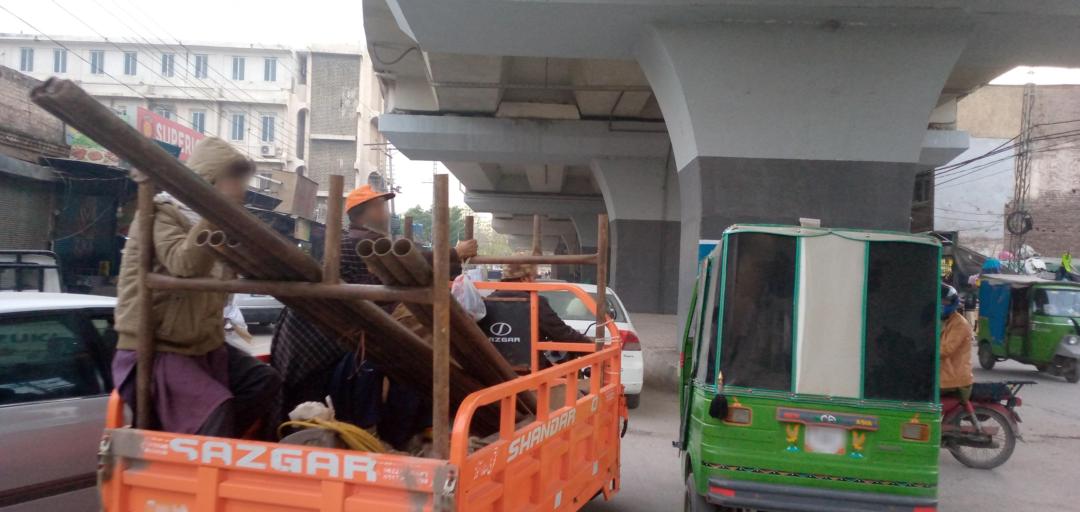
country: PK
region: Khyber Pakhtunkhwa
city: Peshawar
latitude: 33.9955
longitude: 71.5391
